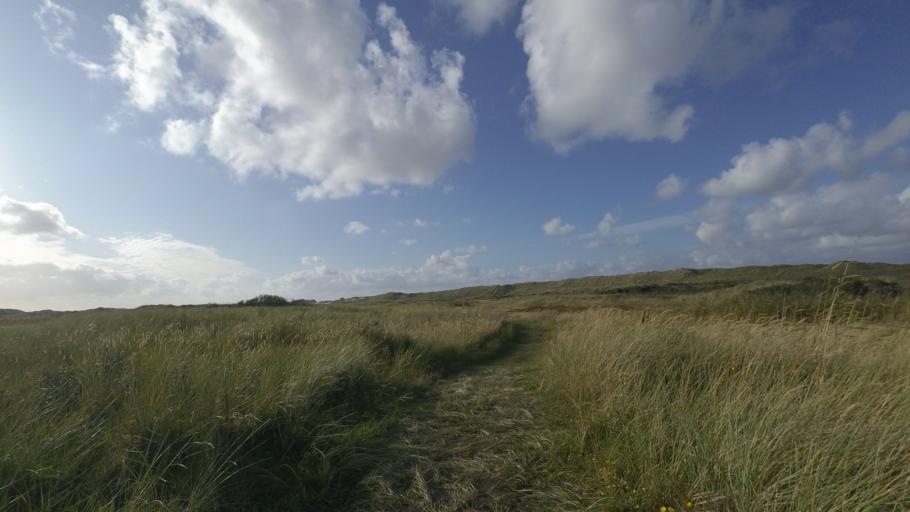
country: NL
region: Friesland
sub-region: Gemeente Dongeradeel
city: Ternaard
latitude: 53.4636
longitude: 5.9152
